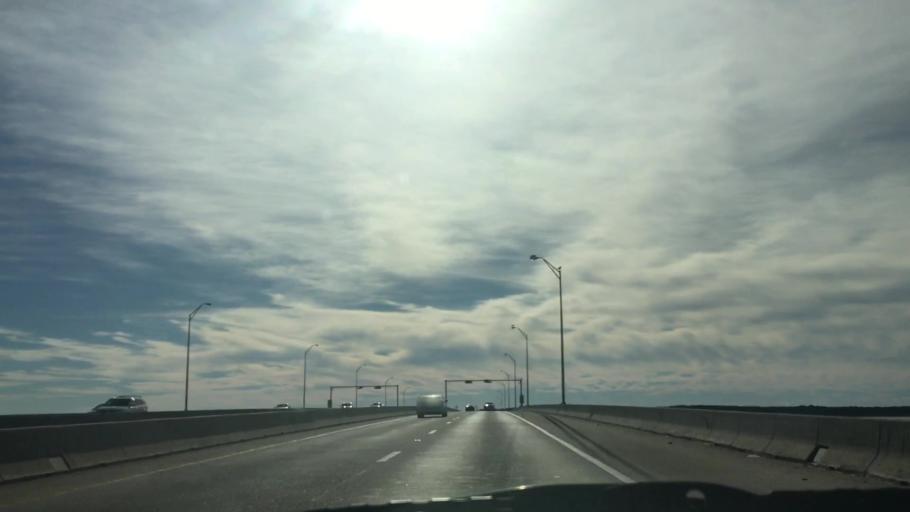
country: US
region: Virginia
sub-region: City of Newport News
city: Newport News
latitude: 36.9114
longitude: -76.4077
